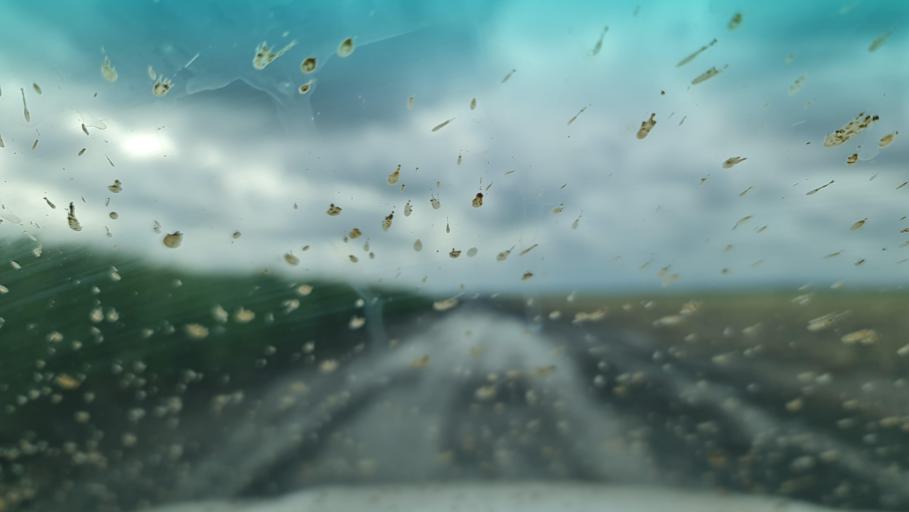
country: EG
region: Luxor
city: Luxor
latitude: 25.4792
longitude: 32.8349
